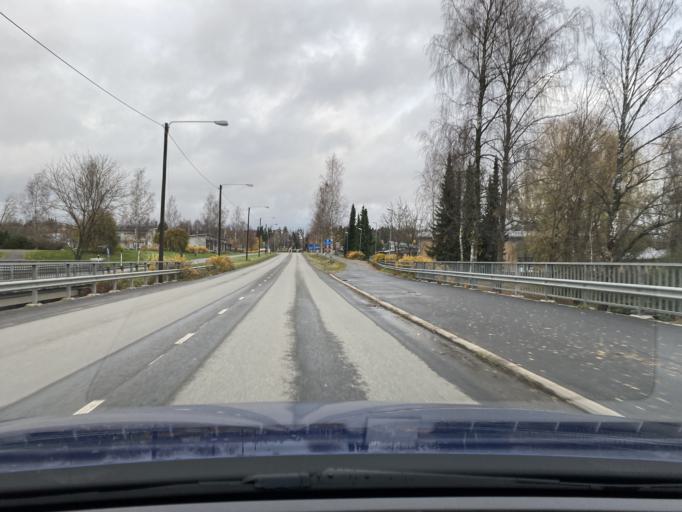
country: FI
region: Pirkanmaa
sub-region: Tampere
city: Lempaeaelae
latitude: 61.3296
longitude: 23.7493
